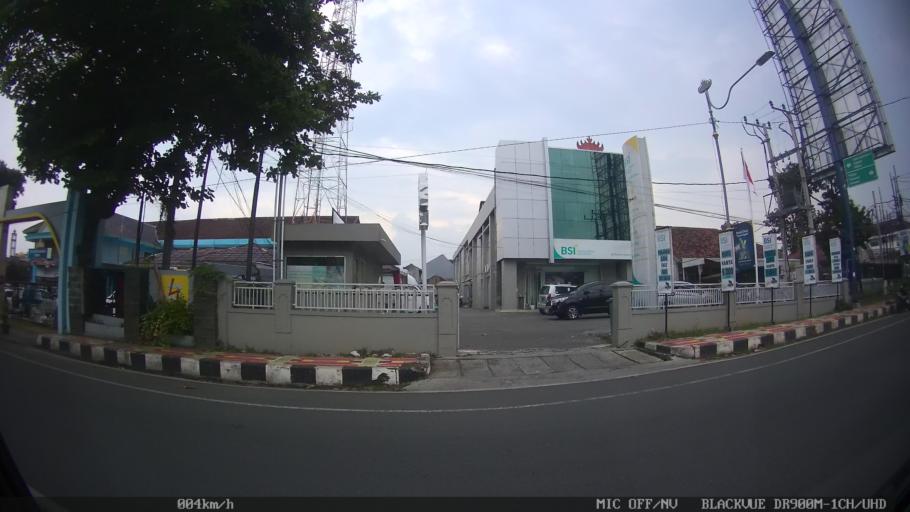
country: ID
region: Lampung
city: Bandarlampung
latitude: -5.4236
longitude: 105.2580
